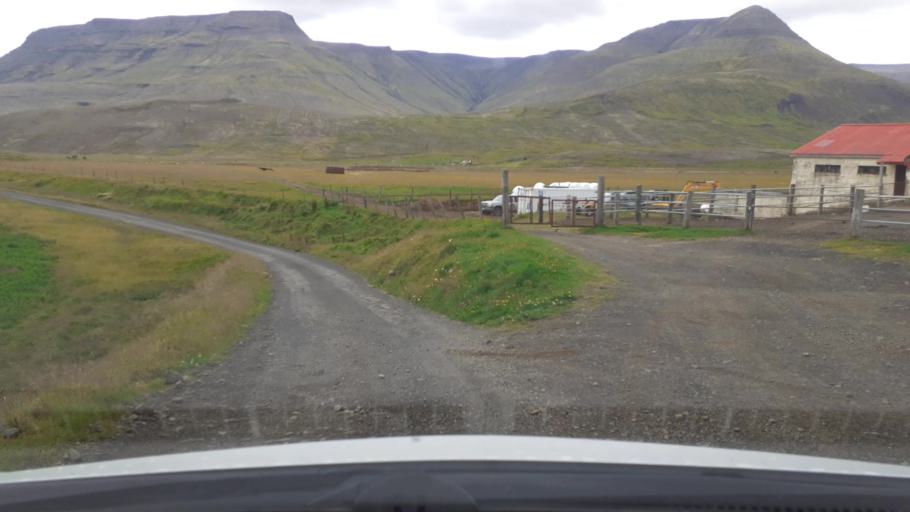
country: IS
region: Capital Region
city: Mosfellsbaer
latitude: 64.2071
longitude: -21.5675
